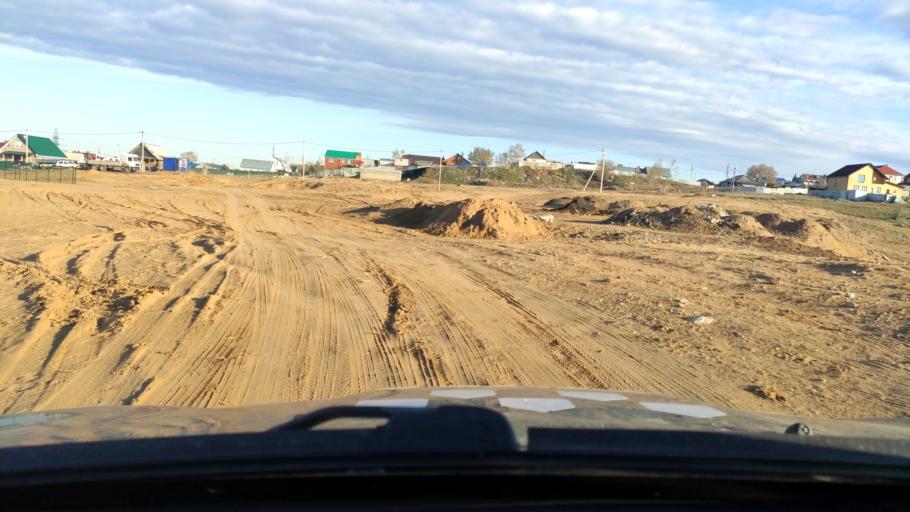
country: RU
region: Samara
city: Zhigulevsk
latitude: 53.4799
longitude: 49.5314
